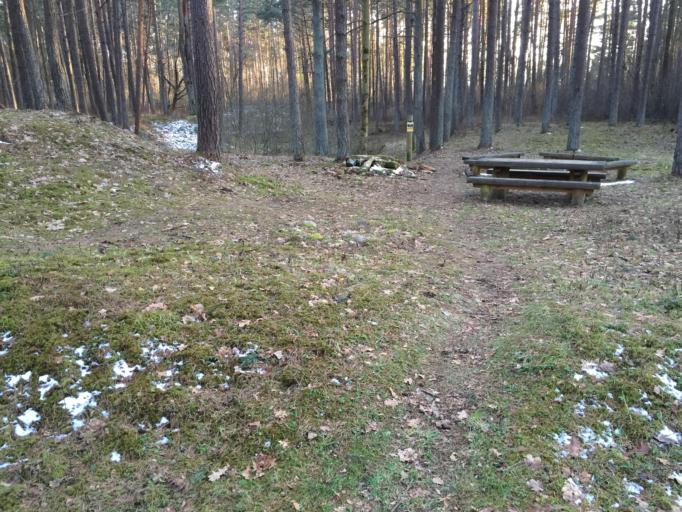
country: LV
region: Kekava
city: Kekava
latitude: 56.8659
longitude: 24.2011
